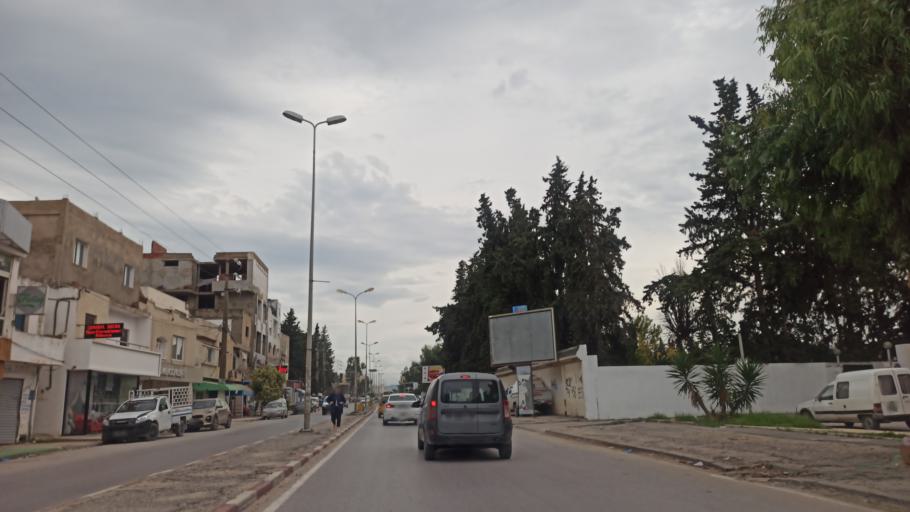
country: TN
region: Ariana
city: Ariana
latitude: 36.8702
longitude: 10.2488
